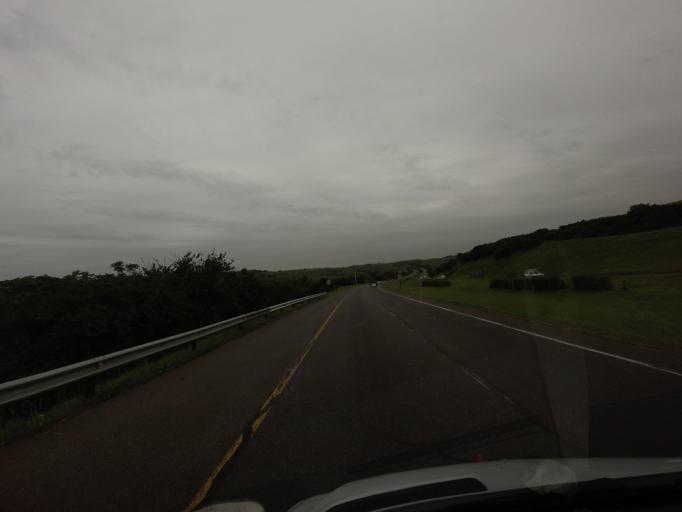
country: ZA
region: KwaZulu-Natal
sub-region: eThekwini Metropolitan Municipality
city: Durban
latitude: -29.6896
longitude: 31.0850
